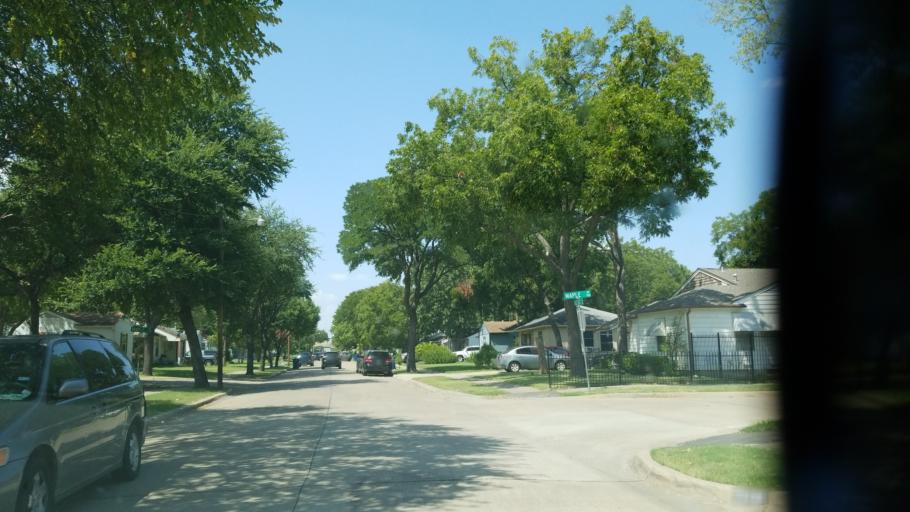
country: US
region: Texas
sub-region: Dallas County
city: Garland
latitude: 32.9185
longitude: -96.6444
